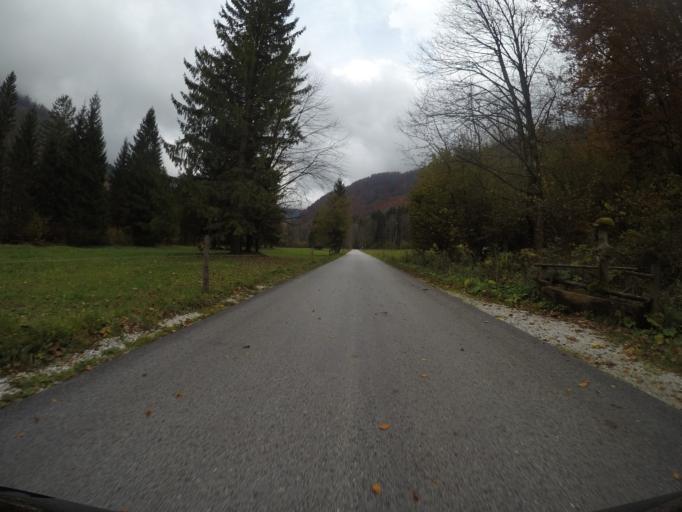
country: SI
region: Jesenice
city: Hrusica
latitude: 46.4223
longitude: 13.9750
